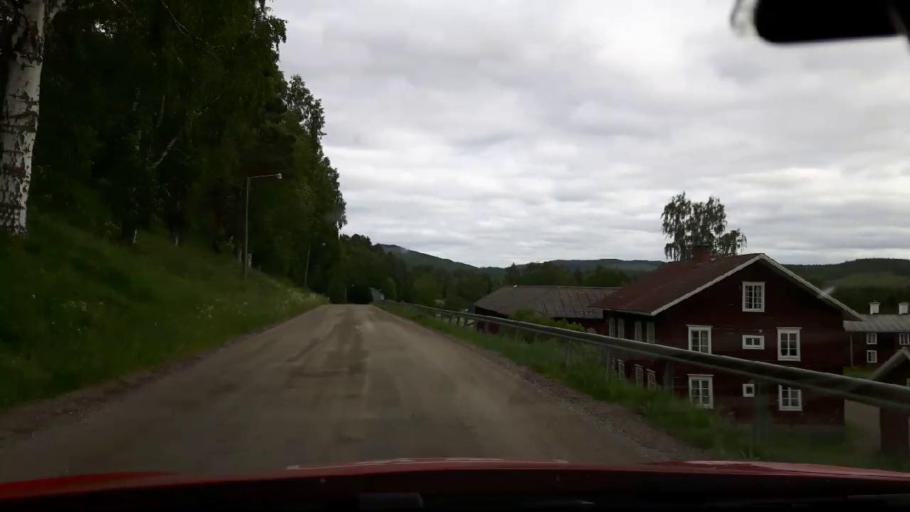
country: SE
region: Jaemtland
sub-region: Ragunda Kommun
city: Hammarstrand
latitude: 63.1616
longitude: 16.2201
